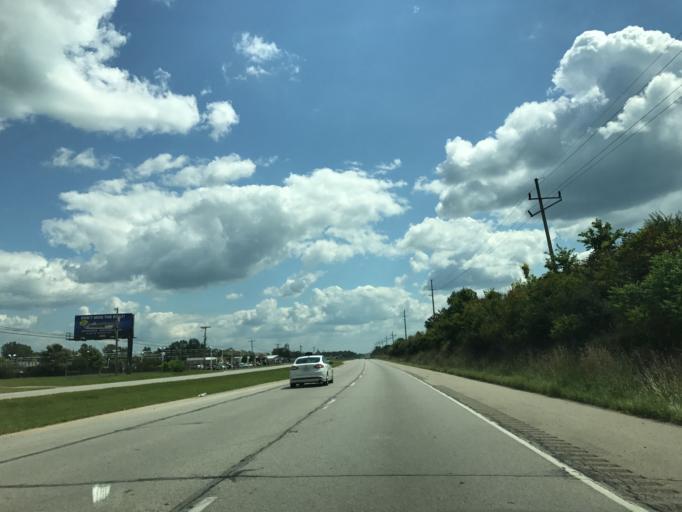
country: US
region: Indiana
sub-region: Kosciusko County
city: Winona Lake
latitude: 41.2231
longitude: -85.7880
